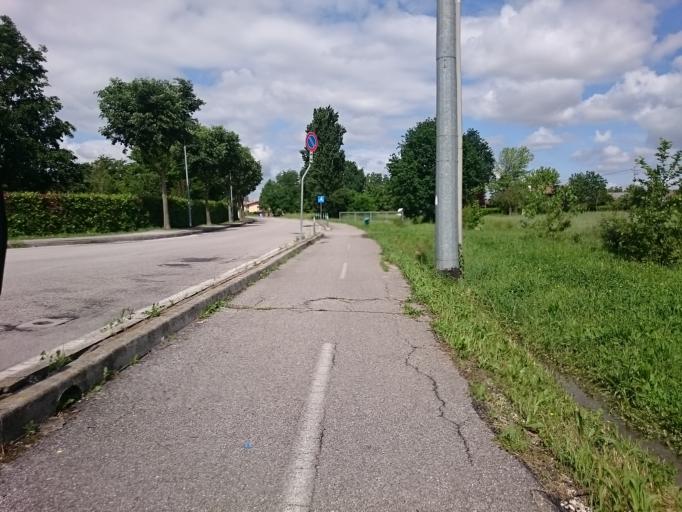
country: IT
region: Veneto
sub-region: Provincia di Padova
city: Mestrino
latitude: 45.4419
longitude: 11.7695
